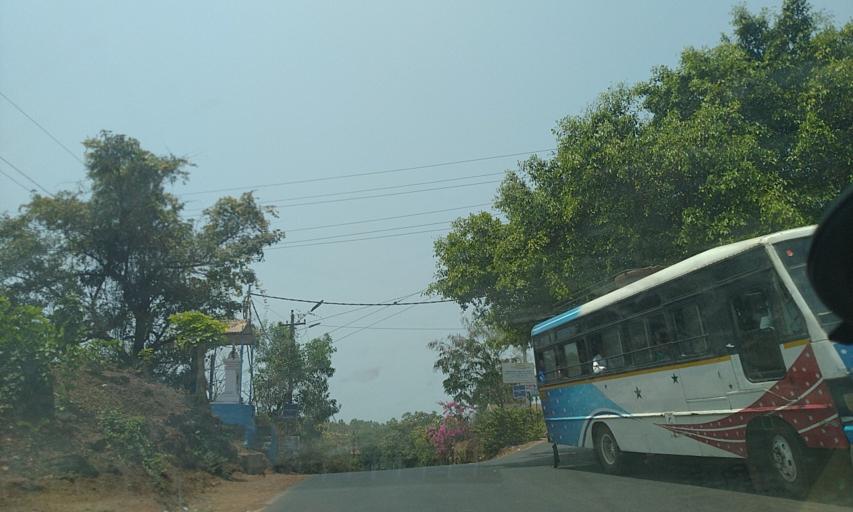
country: IN
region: Goa
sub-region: North Goa
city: Mapuca
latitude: 15.5952
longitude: 73.7973
